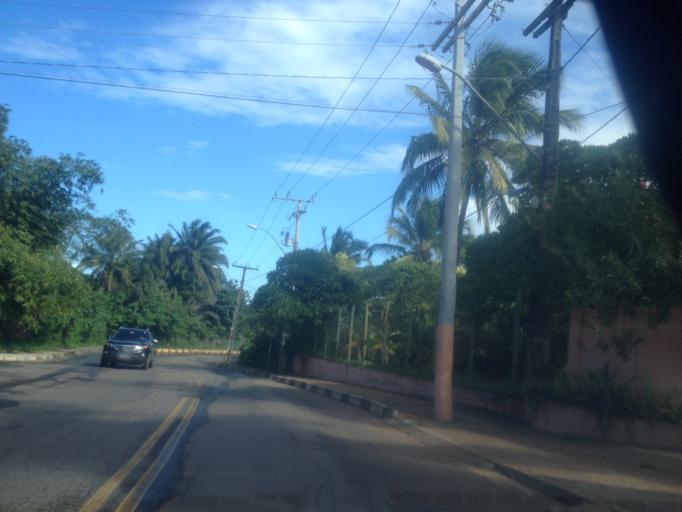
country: BR
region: Bahia
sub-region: Mata De Sao Joao
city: Mata de Sao Joao
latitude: -12.6035
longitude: -38.0408
